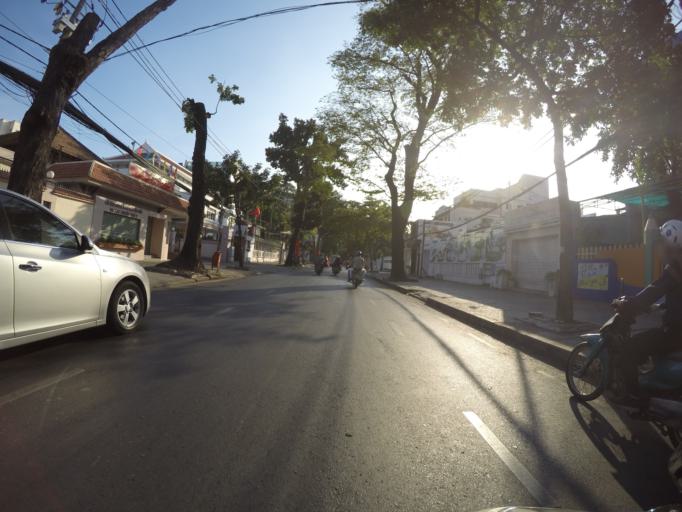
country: VN
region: Ho Chi Minh City
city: Quan Mot
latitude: 10.7873
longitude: 106.6984
